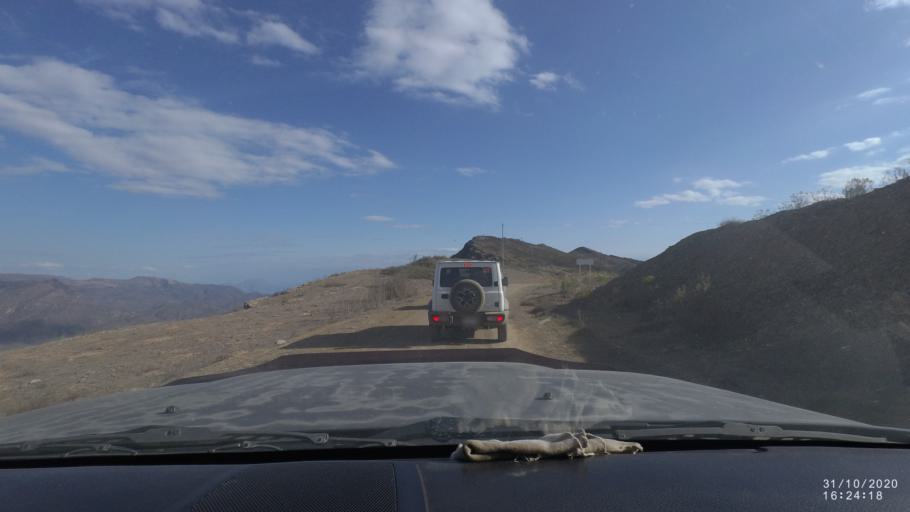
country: BO
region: Chuquisaca
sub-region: Provincia Zudanez
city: Mojocoya
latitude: -18.4005
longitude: -64.5886
